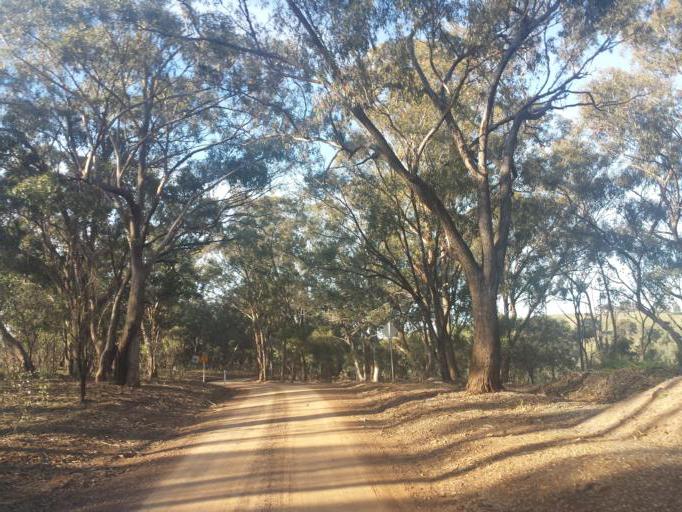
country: AU
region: Victoria
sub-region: Murrindindi
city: Kinglake West
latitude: -37.0267
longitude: 145.2092
